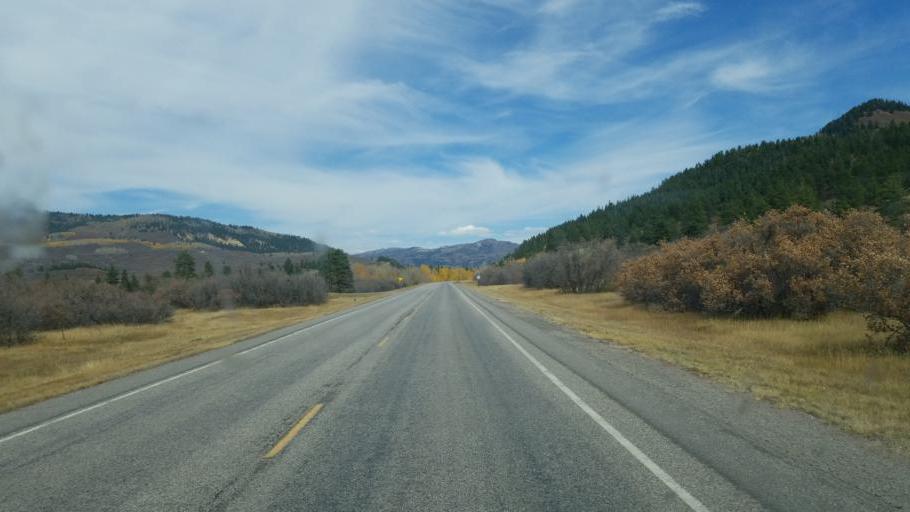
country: US
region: New Mexico
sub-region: Rio Arriba County
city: Chama
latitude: 36.9253
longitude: -106.5596
